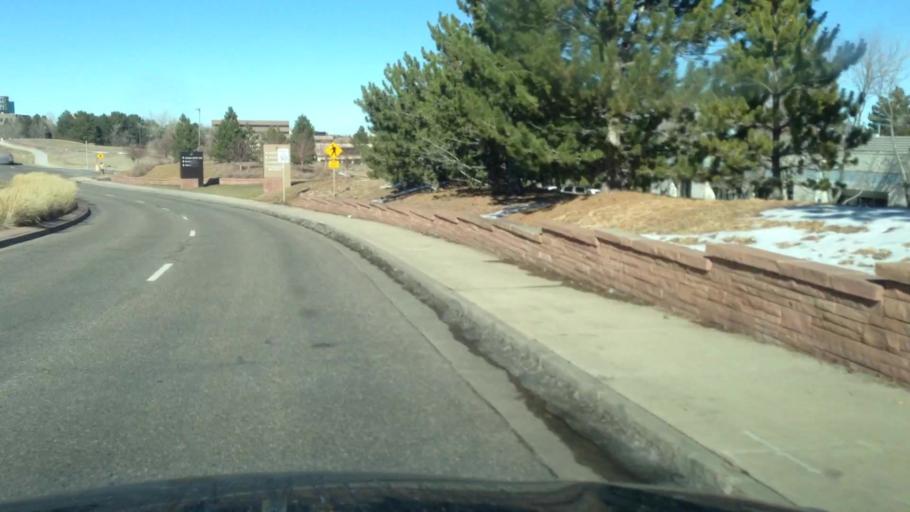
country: US
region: Colorado
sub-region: Douglas County
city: Meridian
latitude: 39.5585
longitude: -104.8647
